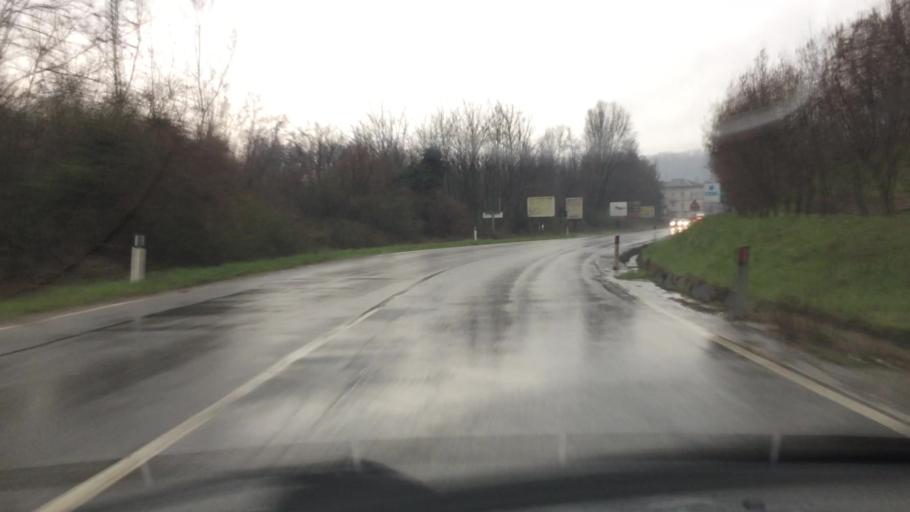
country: IT
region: Lombardy
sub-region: Provincia di Como
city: Montesolaro
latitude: 45.7216
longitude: 9.1034
